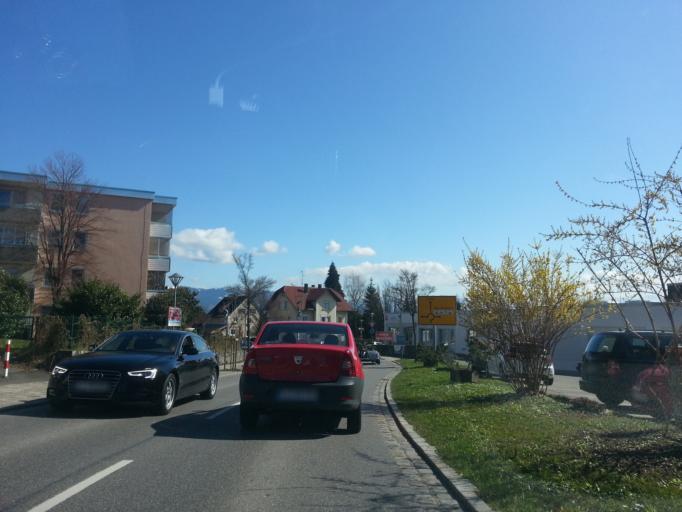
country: DE
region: Bavaria
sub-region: Swabia
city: Bodolz
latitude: 47.5655
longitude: 9.6657
